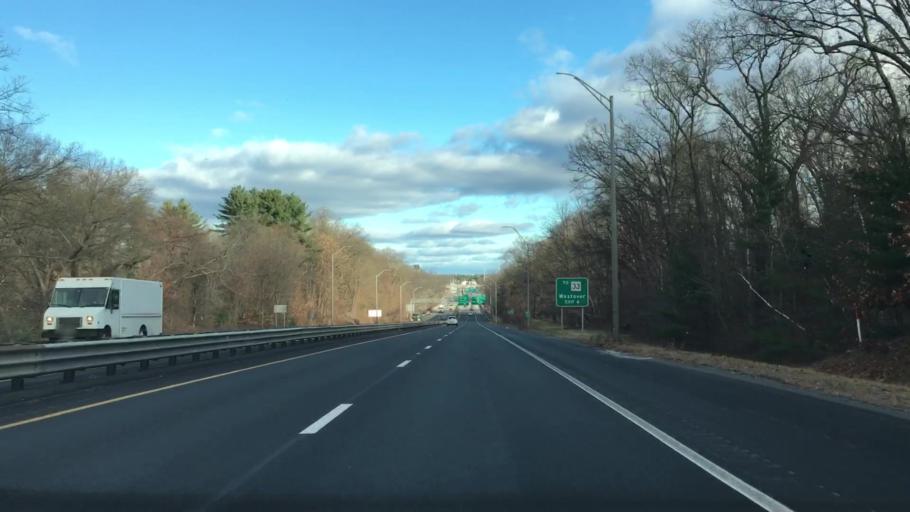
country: US
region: Massachusetts
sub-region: Hampden County
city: Chicopee
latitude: 42.1528
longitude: -72.5492
